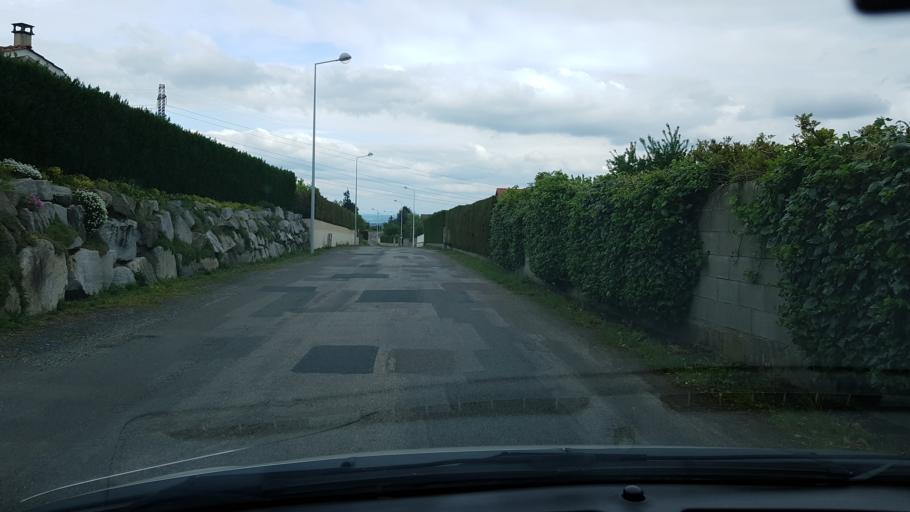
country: FR
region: Rhone-Alpes
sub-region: Departement du Rhone
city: Mornant
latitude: 45.6456
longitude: 4.6889
